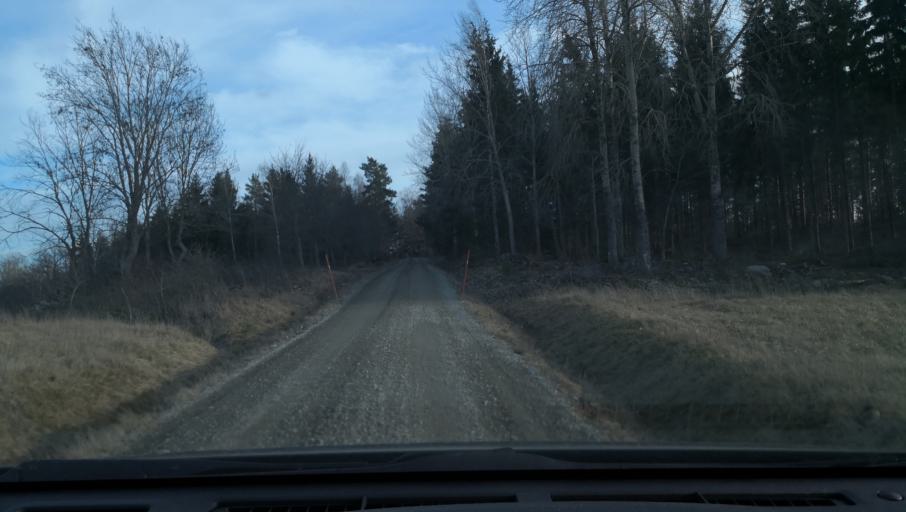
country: SE
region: Uppsala
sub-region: Enkopings Kommun
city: Dalby
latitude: 59.4824
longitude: 17.2517
